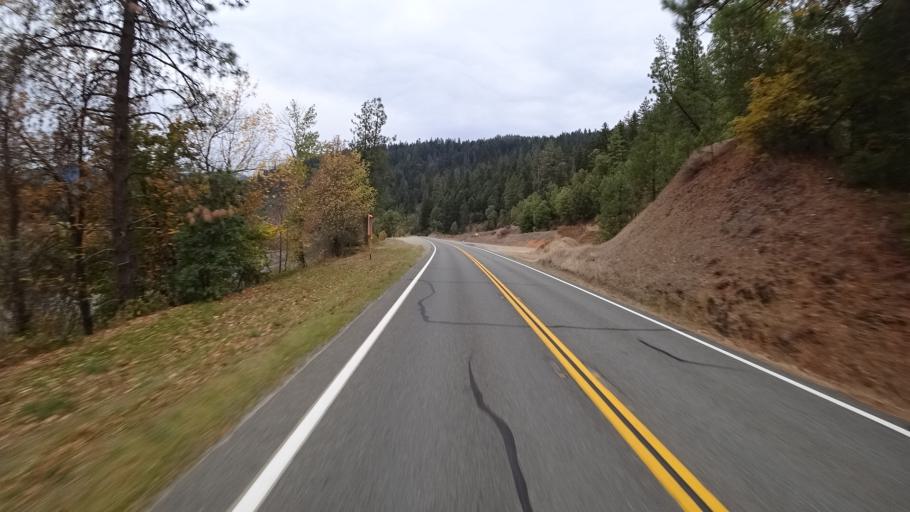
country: US
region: California
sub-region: Siskiyou County
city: Happy Camp
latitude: 41.8102
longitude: -123.3522
